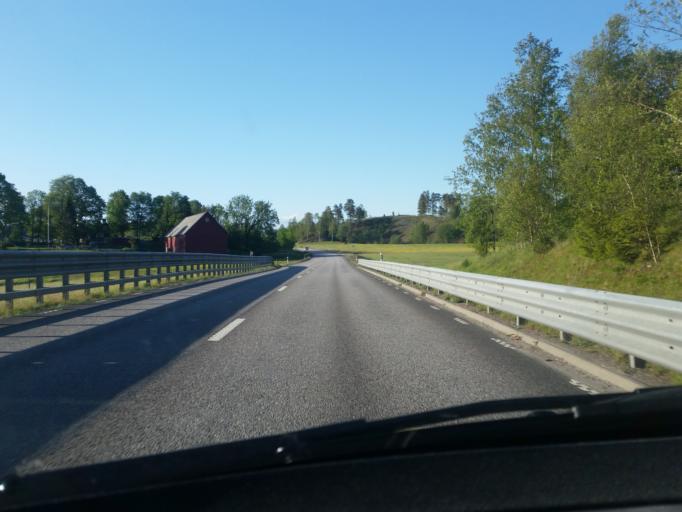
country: SE
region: Vaestra Goetaland
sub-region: Fargelanda Kommun
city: Faergelanda
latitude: 58.5483
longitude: 11.9911
